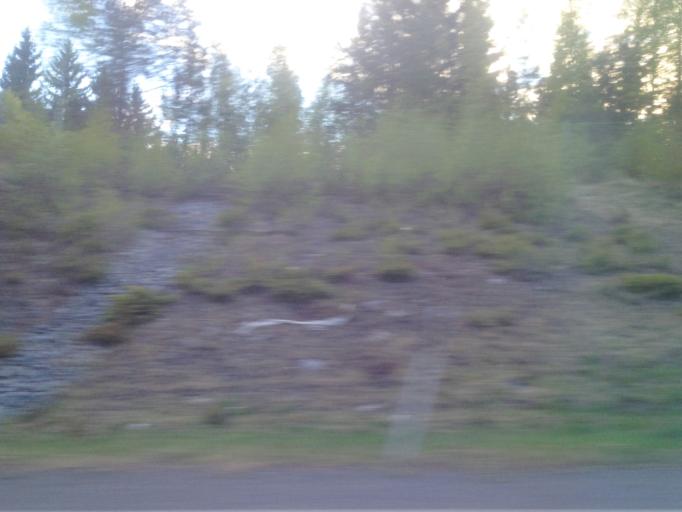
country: FI
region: Pirkanmaa
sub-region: Etelae-Pirkanmaa
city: Toijala
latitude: 61.2360
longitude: 23.8369
